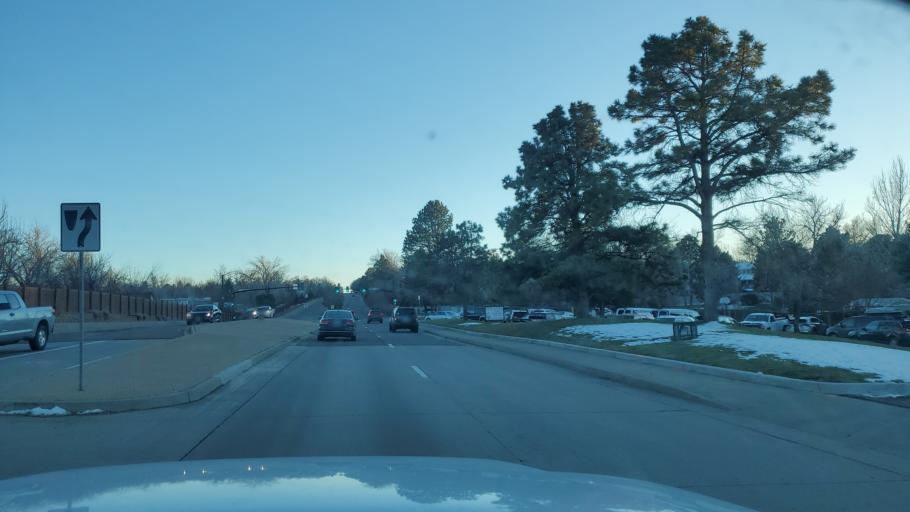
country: US
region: Colorado
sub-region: Arapahoe County
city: Castlewood
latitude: 39.5928
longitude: -104.9043
